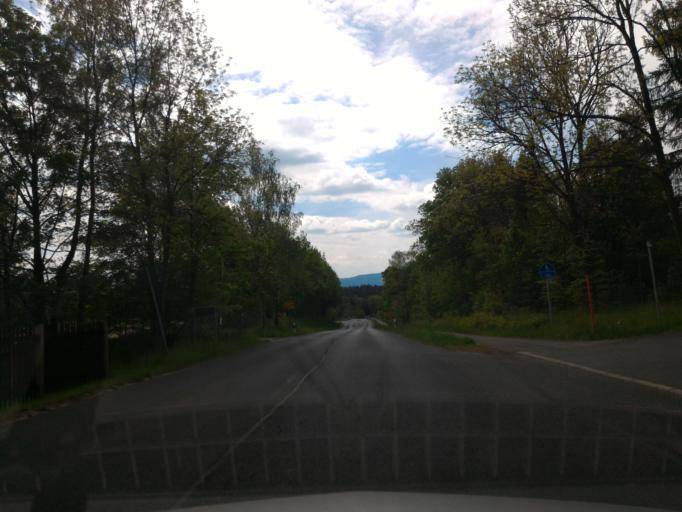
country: DE
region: Saxony
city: Neugersdorf
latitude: 50.9671
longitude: 14.5994
